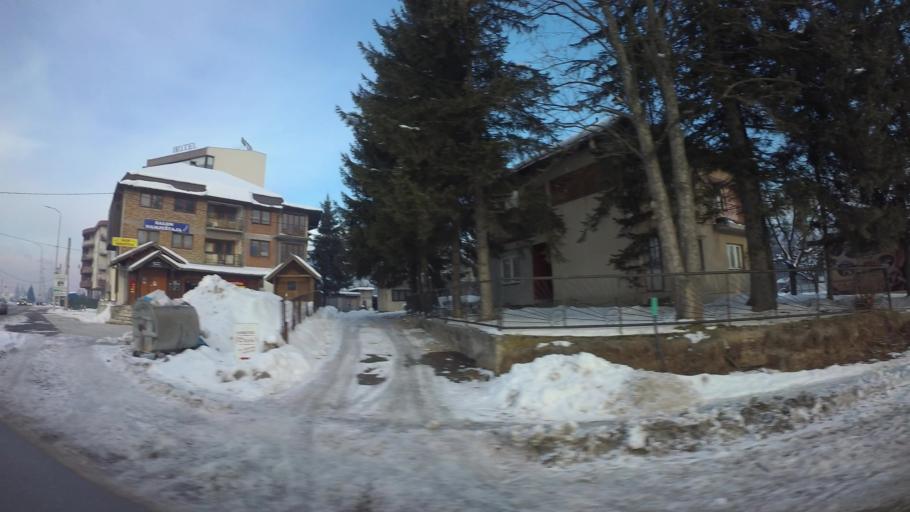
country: BA
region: Federation of Bosnia and Herzegovina
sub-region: Kanton Sarajevo
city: Sarajevo
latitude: 43.8274
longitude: 18.3666
